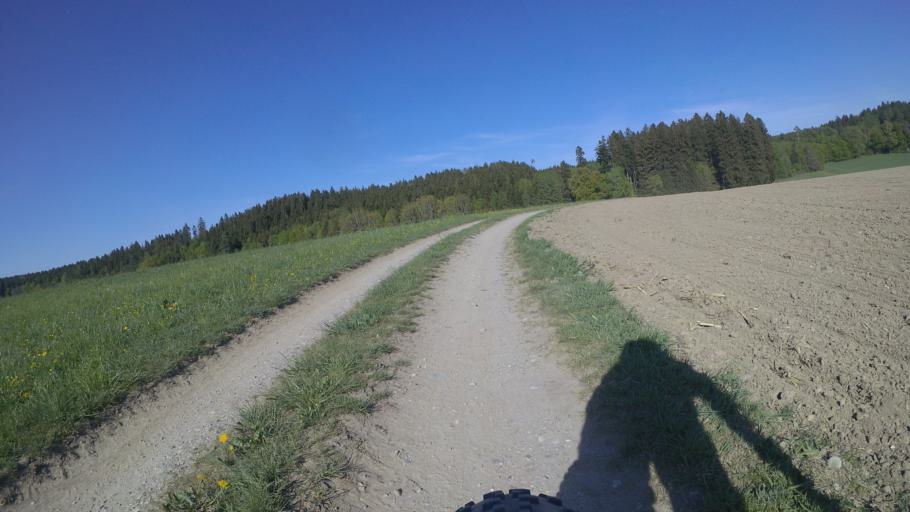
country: DE
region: Bavaria
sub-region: Upper Bavaria
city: Traunreut
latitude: 47.9363
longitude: 12.5638
